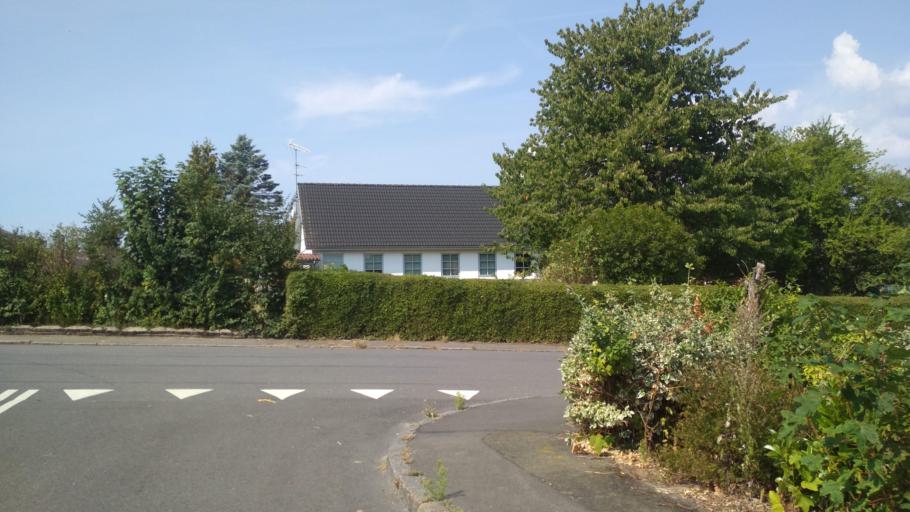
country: DK
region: Capital Region
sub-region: Bornholm Kommune
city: Akirkeby
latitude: 55.0674
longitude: 14.9261
